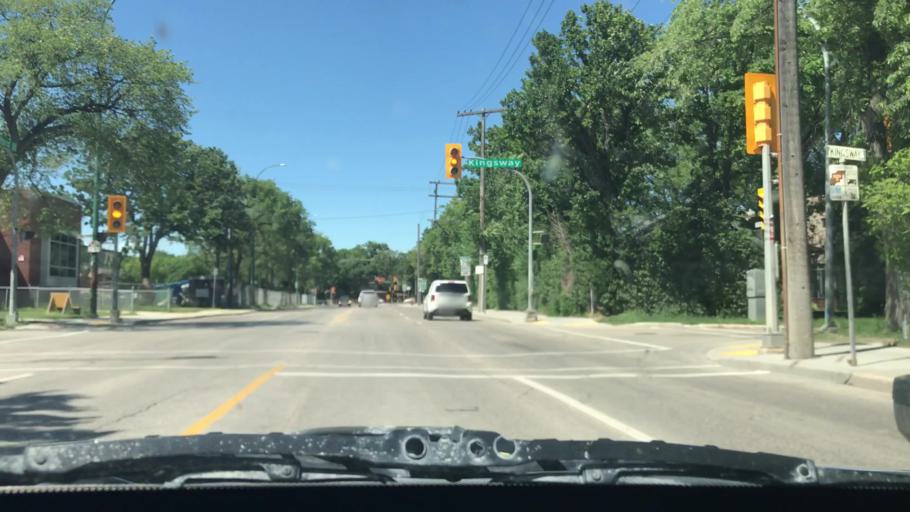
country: CA
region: Manitoba
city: Winnipeg
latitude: 49.8733
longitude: -97.1657
